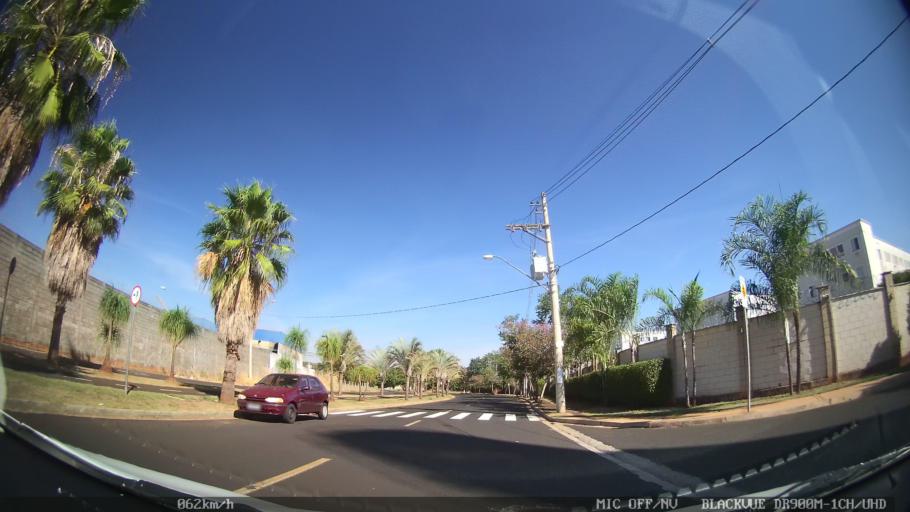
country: BR
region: Sao Paulo
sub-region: Ribeirao Preto
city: Ribeirao Preto
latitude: -21.2216
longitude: -47.7624
